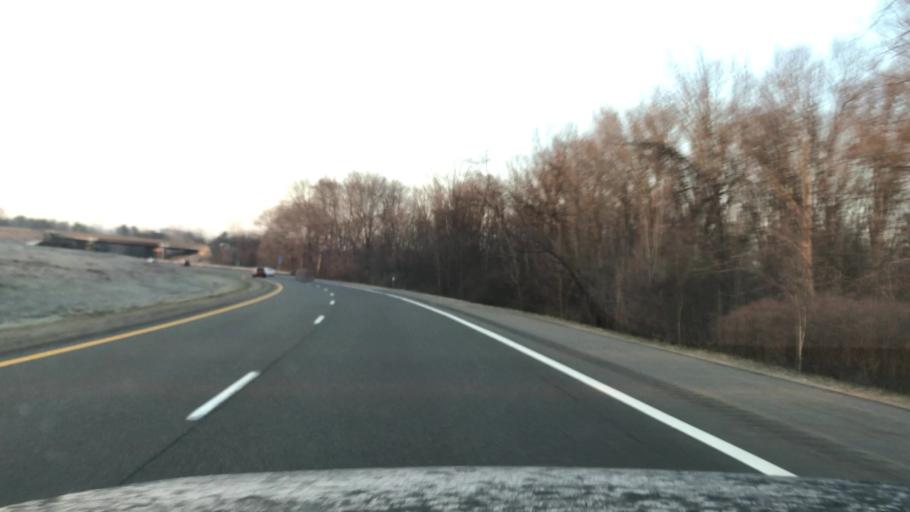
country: US
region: Michigan
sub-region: Kent County
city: East Grand Rapids
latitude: 42.9796
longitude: -85.6052
